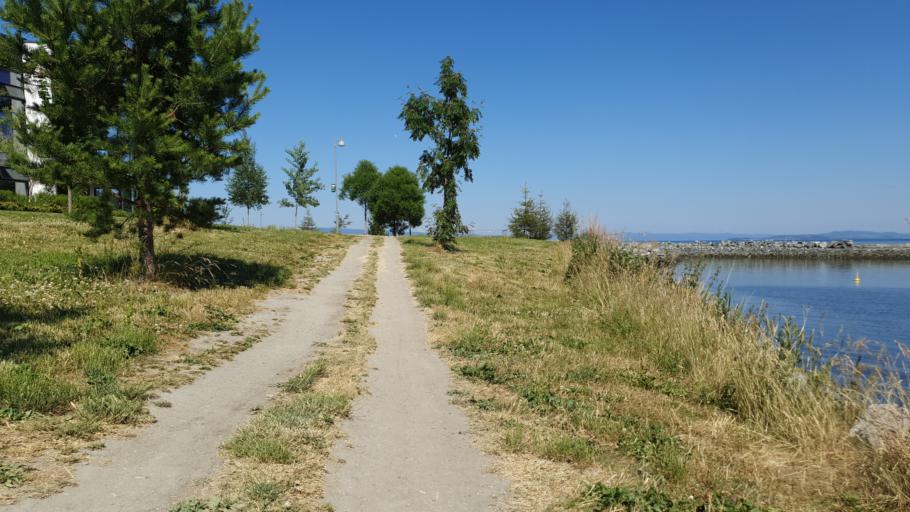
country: NO
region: Sor-Trondelag
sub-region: Trondheim
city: Trondheim
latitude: 63.4348
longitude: 10.5114
